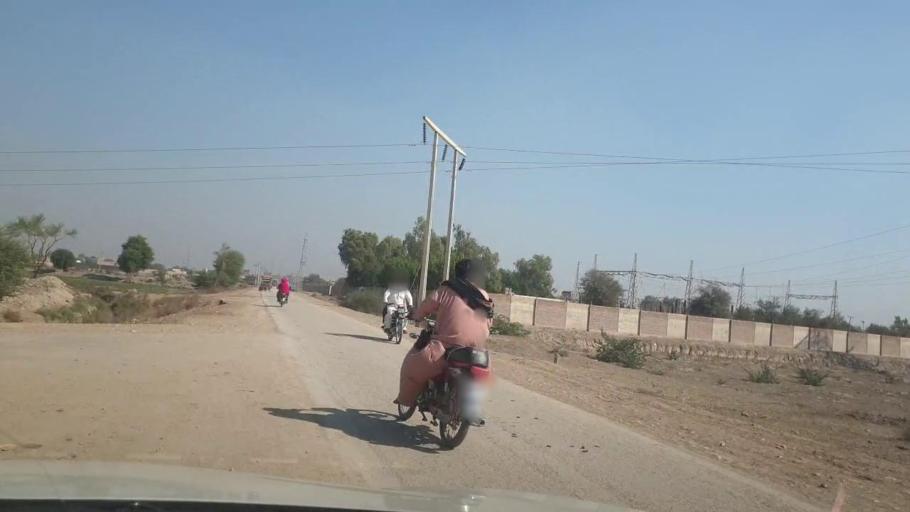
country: PK
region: Sindh
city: Bhan
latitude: 26.5482
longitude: 67.7112
